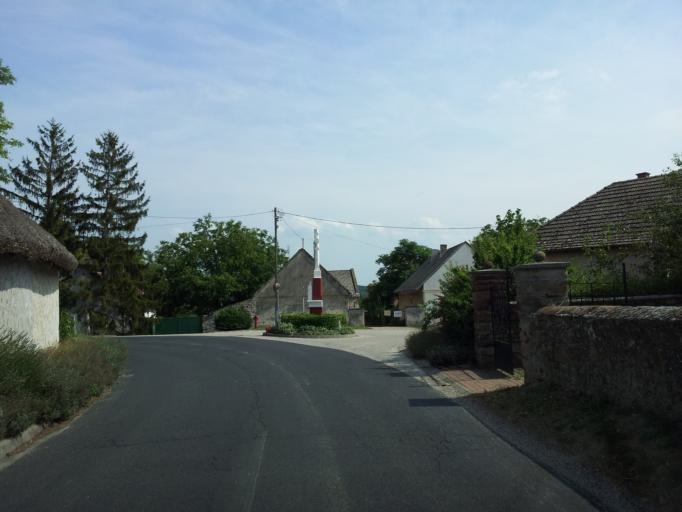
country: HU
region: Veszprem
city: Badacsonytomaj
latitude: 46.8506
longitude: 17.5586
